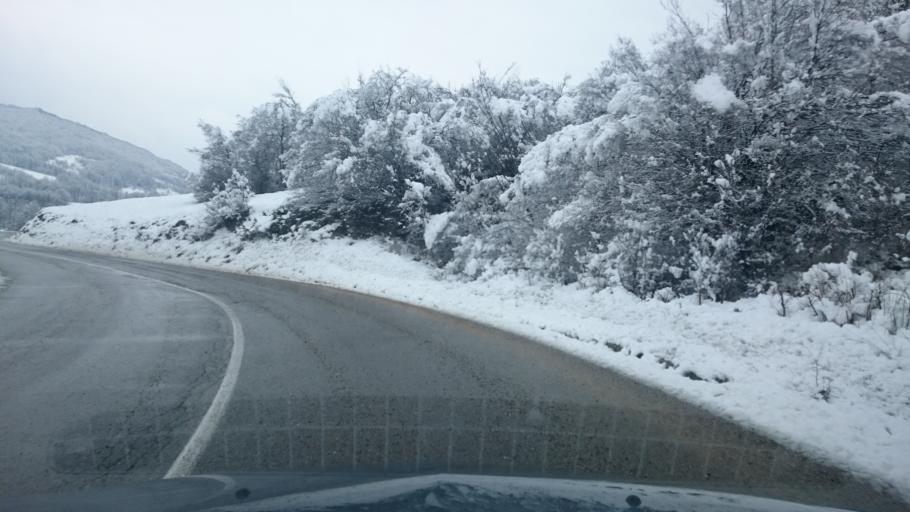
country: BA
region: Republika Srpska
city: Starcevica
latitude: 44.6396
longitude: 17.2385
